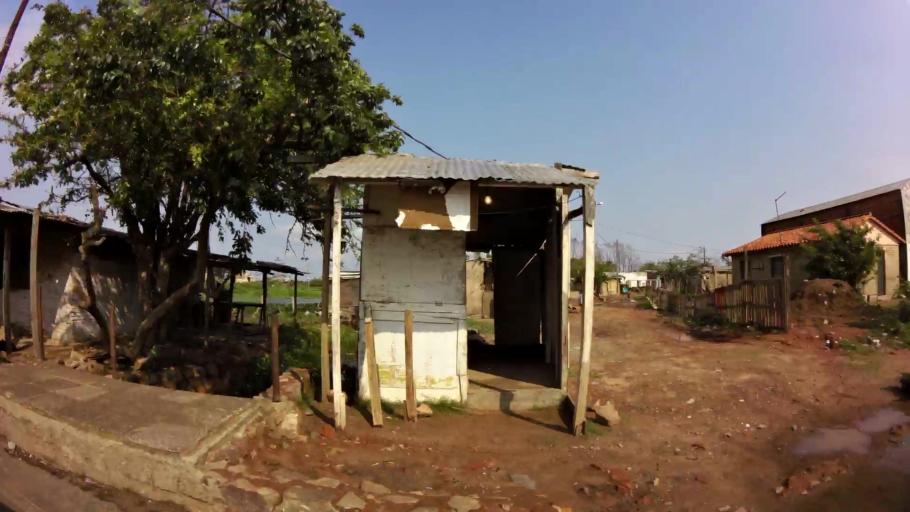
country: PY
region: Asuncion
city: Asuncion
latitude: -25.3115
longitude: -57.6673
